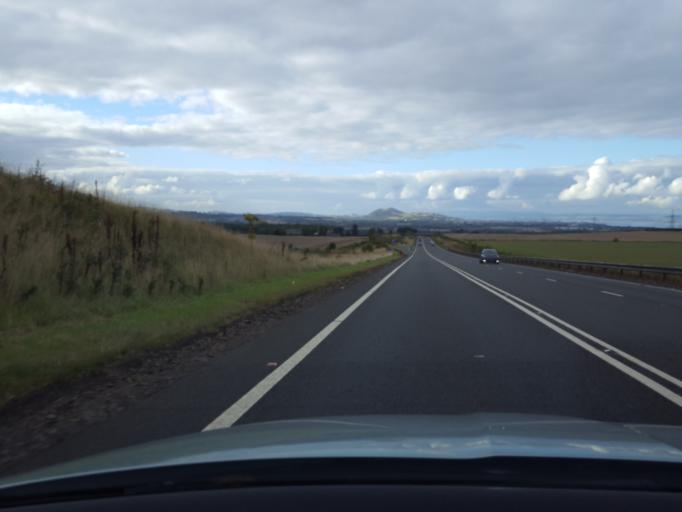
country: GB
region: Scotland
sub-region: Fife
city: Pathhead
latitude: 55.8963
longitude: -3.0095
